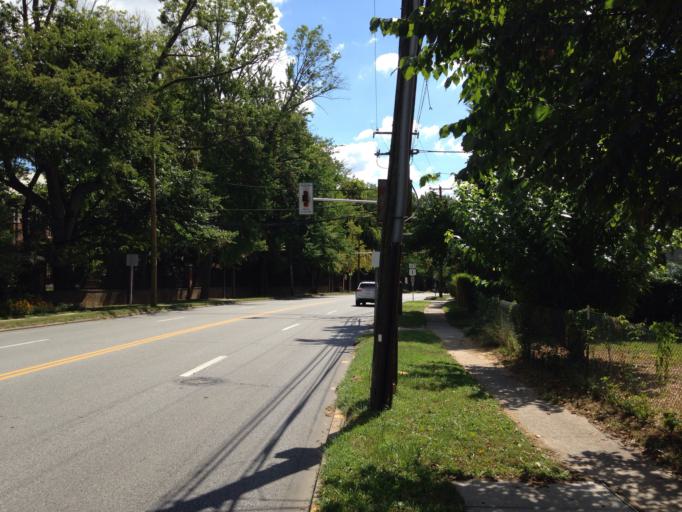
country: US
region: Pennsylvania
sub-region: Montgomery County
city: Penn Wynne
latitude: 39.9829
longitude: -75.2717
